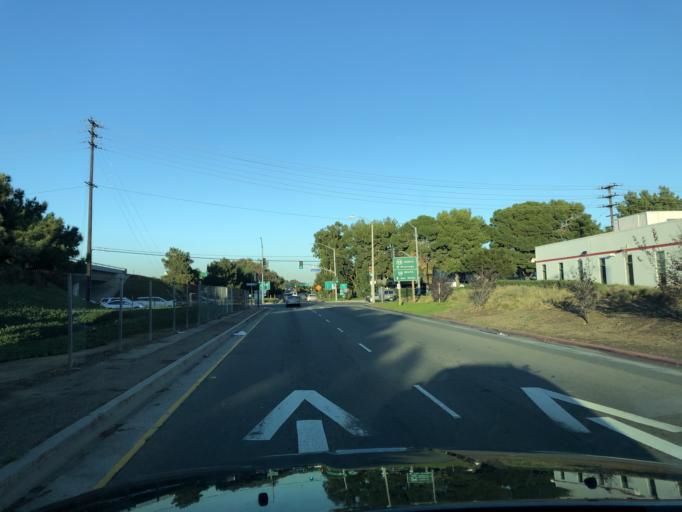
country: US
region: California
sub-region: Orange County
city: Irvine
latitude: 33.6812
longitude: -117.8774
